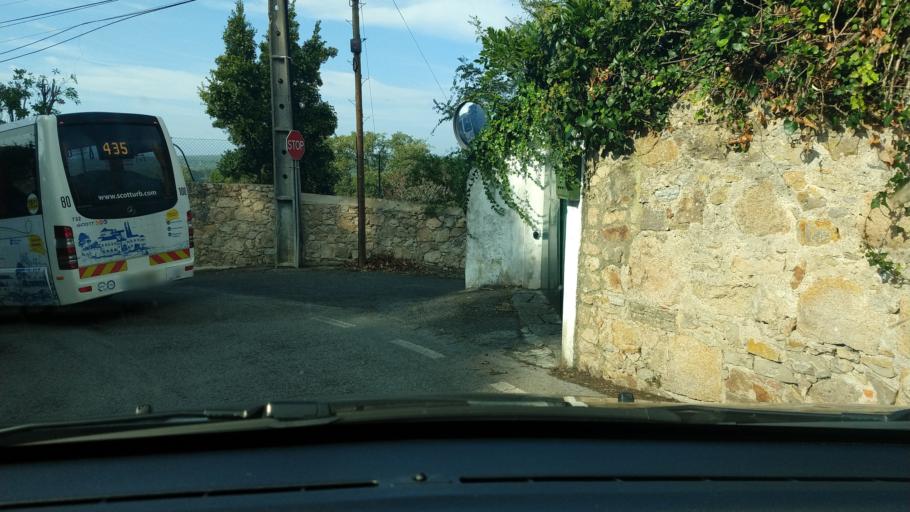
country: PT
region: Lisbon
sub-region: Sintra
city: Colares
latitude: 38.7965
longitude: -9.4296
